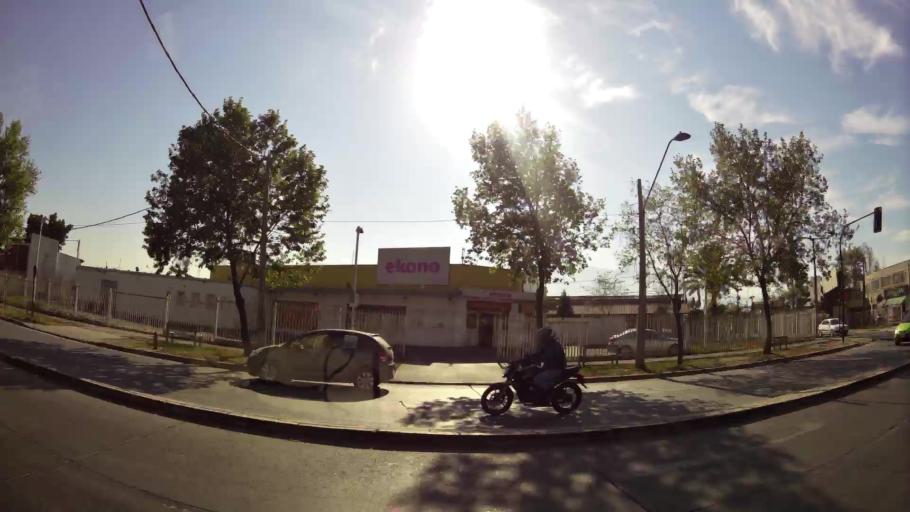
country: CL
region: Santiago Metropolitan
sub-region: Provincia de Santiago
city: La Pintana
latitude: -33.5621
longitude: -70.6002
